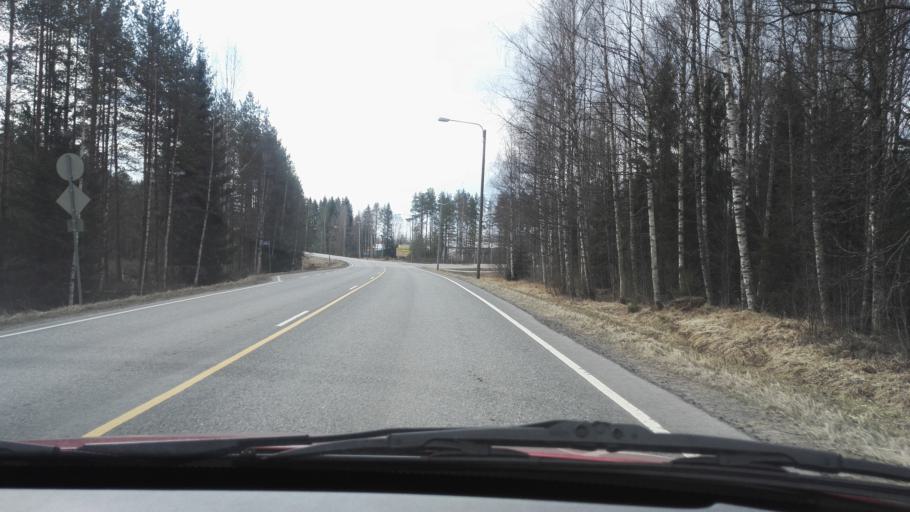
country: FI
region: Central Finland
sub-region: Jyvaeskylae
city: Petaejaevesi
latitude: 62.2686
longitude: 25.1709
